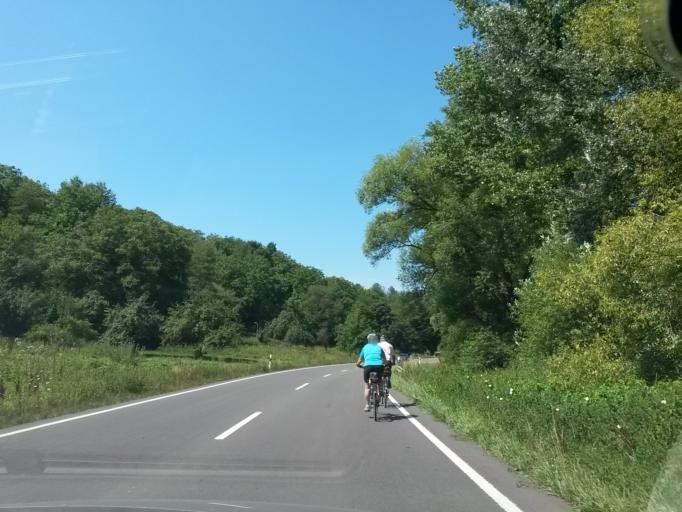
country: DE
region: Baden-Wuerttemberg
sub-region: Karlsruhe Region
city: Neuenburg
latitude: 48.8984
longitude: 8.5895
